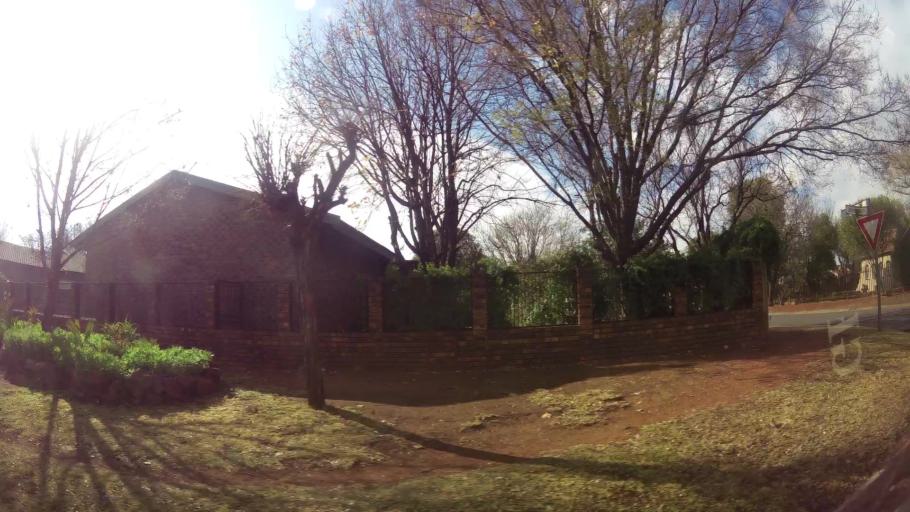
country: ZA
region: Gauteng
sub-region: Sedibeng District Municipality
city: Meyerton
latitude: -26.5527
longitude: 28.0353
